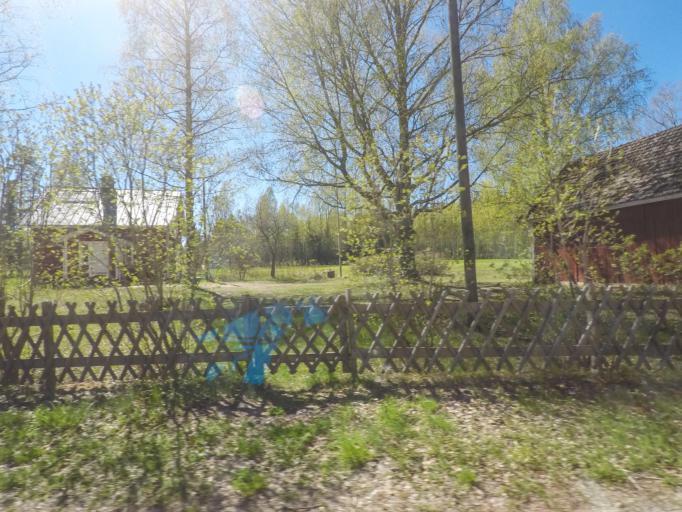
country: FI
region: Uusimaa
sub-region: Helsinki
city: Sammatti
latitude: 60.3347
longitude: 23.8016
